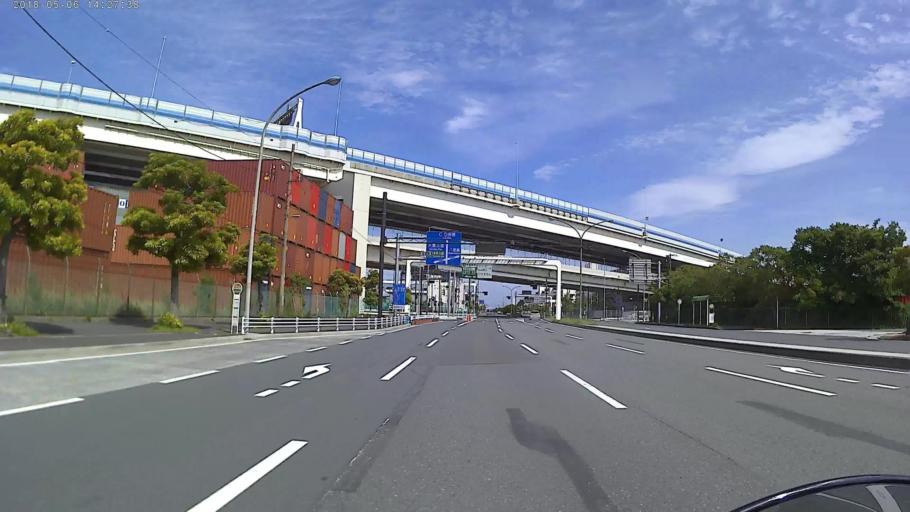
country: JP
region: Kanagawa
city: Yokohama
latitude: 35.4317
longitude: 139.6698
